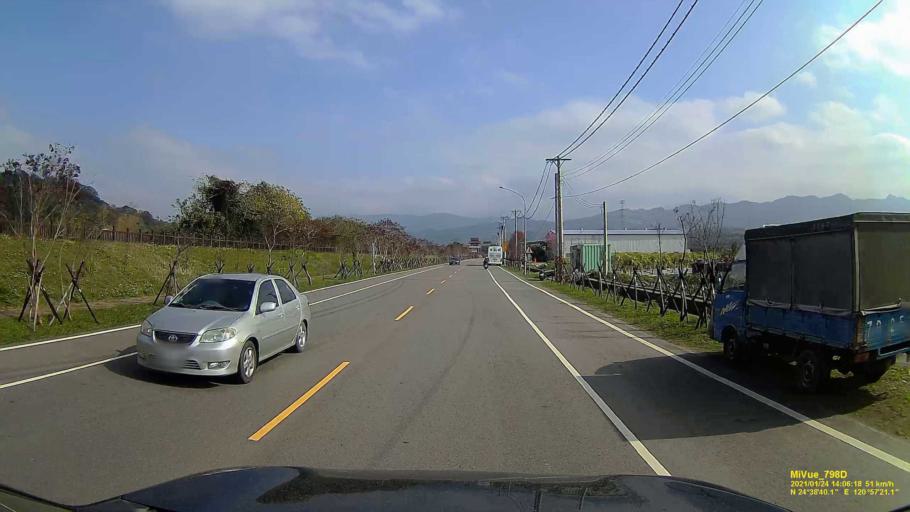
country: TW
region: Taiwan
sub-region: Miaoli
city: Miaoli
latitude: 24.6444
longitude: 120.9561
